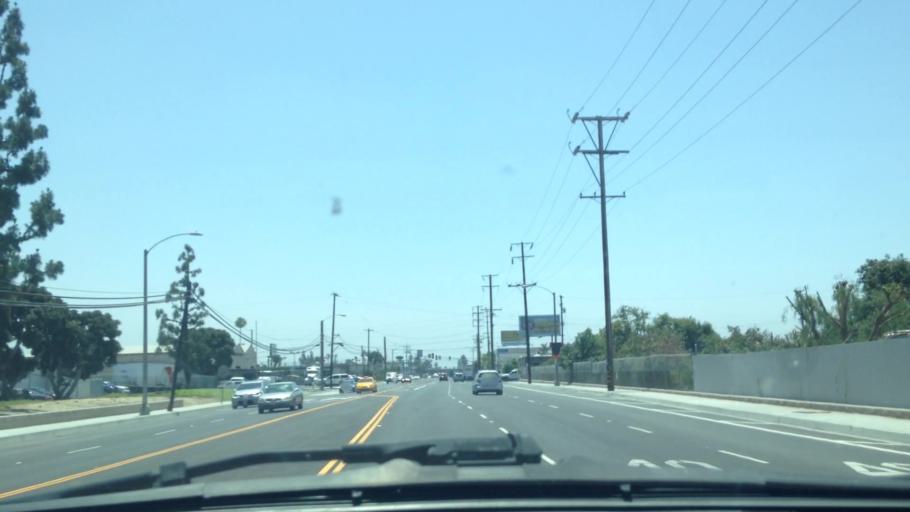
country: US
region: California
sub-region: Orange County
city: Placentia
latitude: 33.8625
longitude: -117.8895
